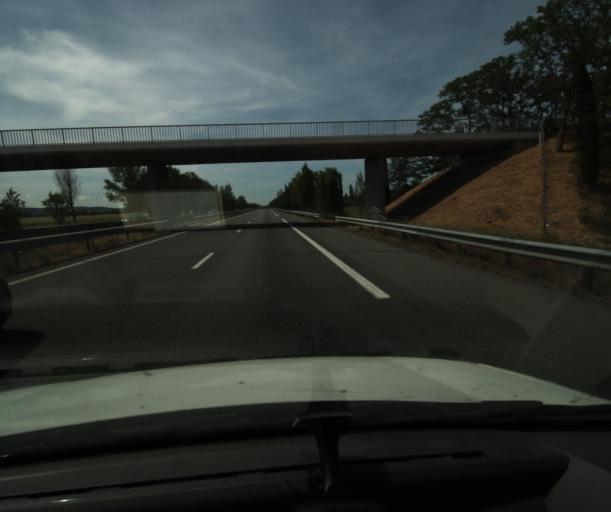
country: FR
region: Languedoc-Roussillon
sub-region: Departement de l'Aude
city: Saint-Martin-Lalande
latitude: 43.2666
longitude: 2.0123
